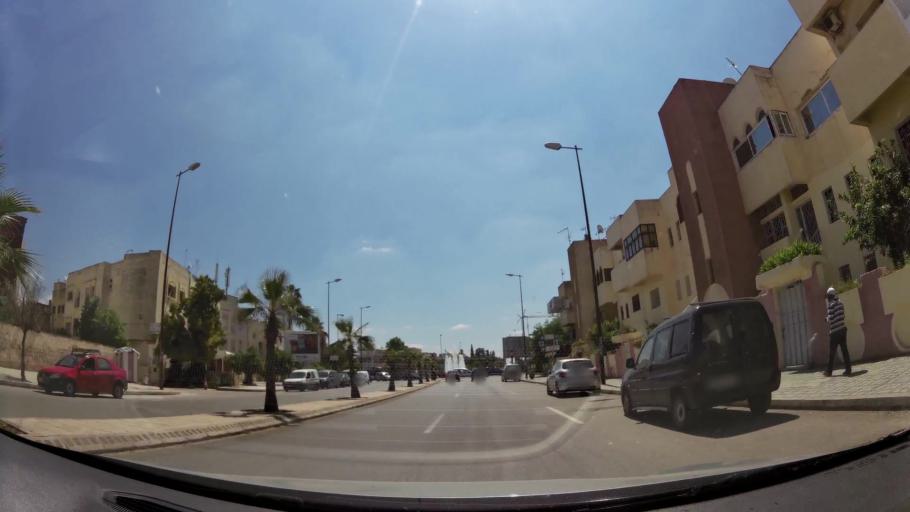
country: MA
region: Fes-Boulemane
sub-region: Fes
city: Fes
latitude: 34.0241
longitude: -5.0170
